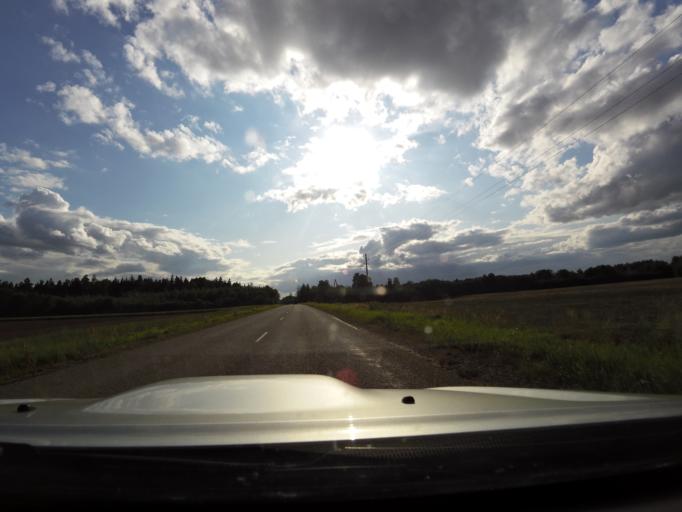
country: LV
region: Nereta
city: Nereta
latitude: 56.1904
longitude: 25.4215
